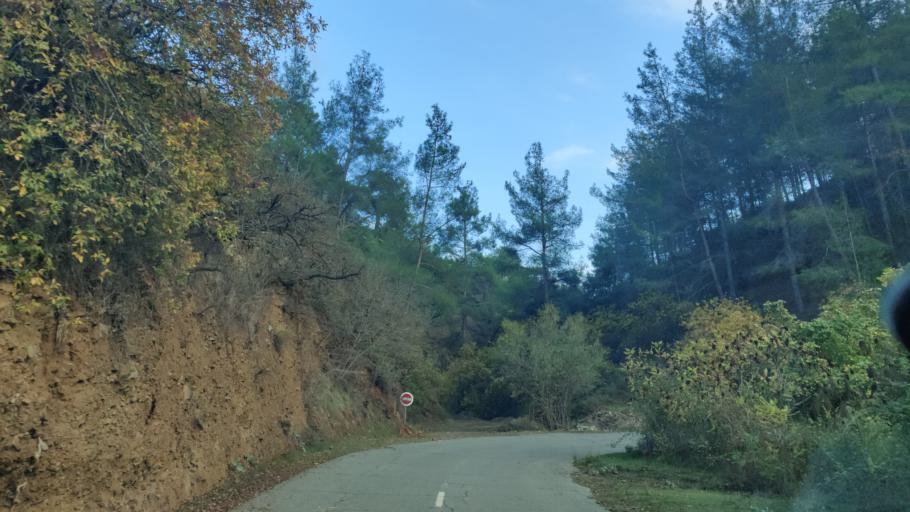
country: CY
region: Lefkosia
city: Lefka
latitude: 35.0641
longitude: 32.7363
